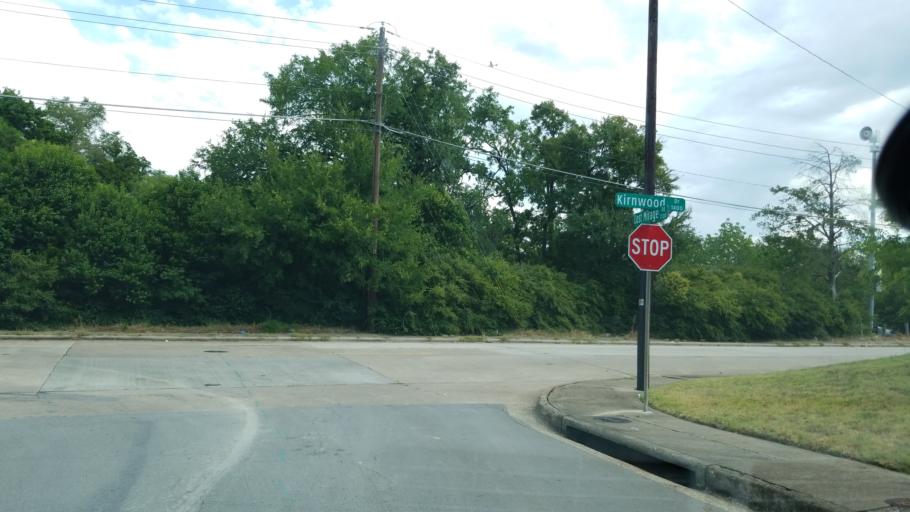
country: US
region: Texas
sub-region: Dallas County
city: Duncanville
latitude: 32.6547
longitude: -96.8460
